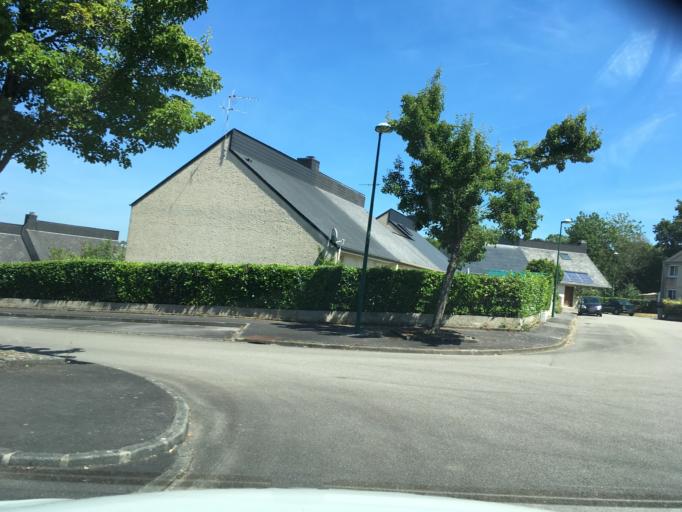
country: FR
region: Brittany
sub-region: Departement du Finistere
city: Quimper
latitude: 47.9988
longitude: -4.1206
